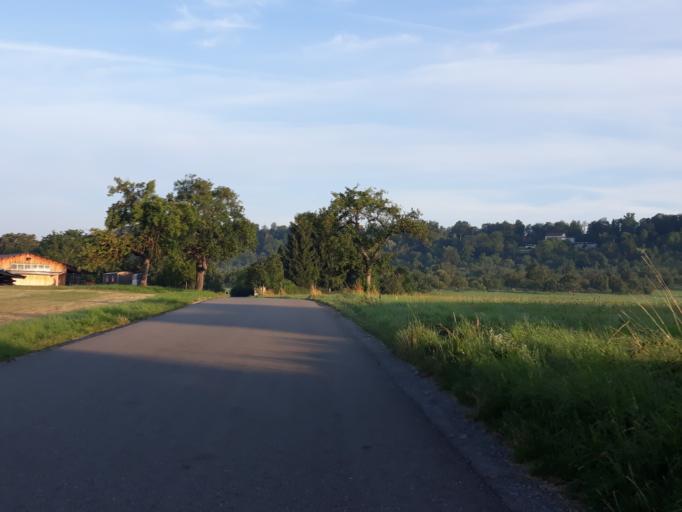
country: DE
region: Baden-Wuerttemberg
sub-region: Regierungsbezirk Stuttgart
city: Schonaich
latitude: 48.6605
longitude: 9.0516
